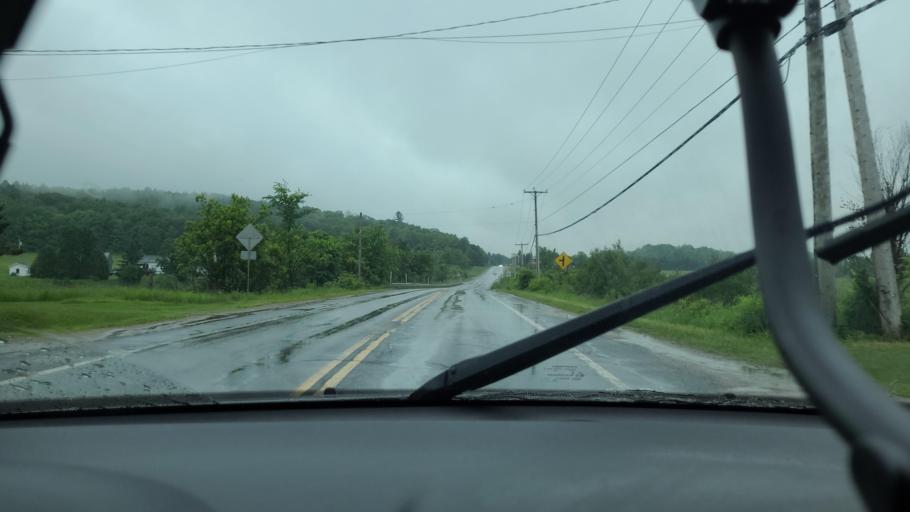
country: CA
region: Quebec
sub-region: Outaouais
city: Saint-Andre-Avellin
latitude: 45.7127
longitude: -75.0556
